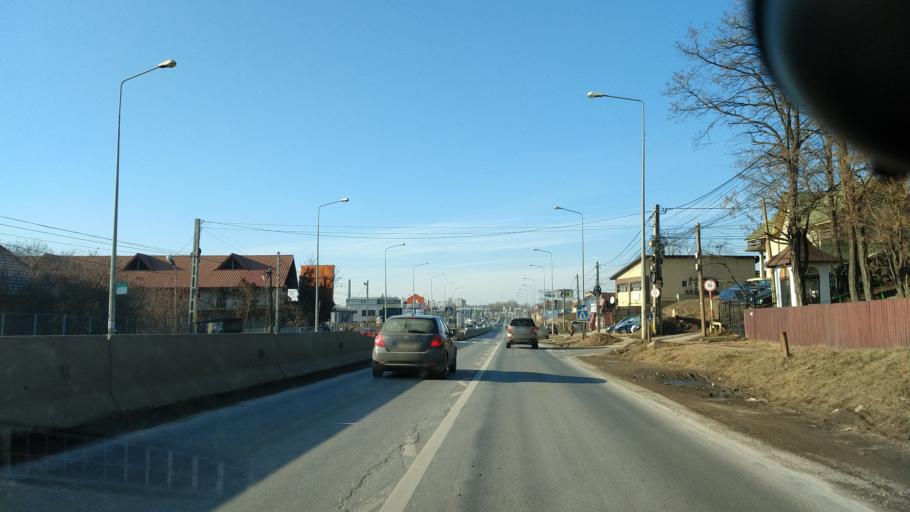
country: RO
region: Iasi
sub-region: Comuna Valea Lupului
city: Valea Lupului
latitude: 47.1738
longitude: 27.5068
